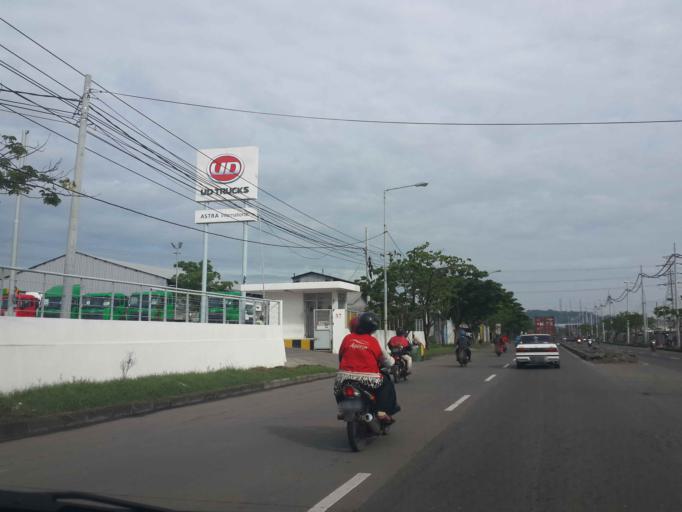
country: ID
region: East Java
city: Kebomas
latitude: -7.2025
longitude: 112.6494
